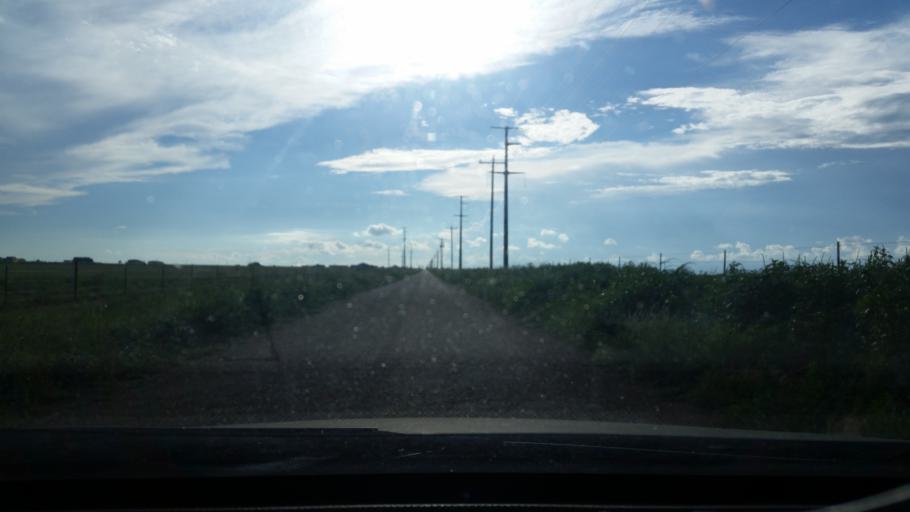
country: US
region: New Mexico
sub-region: Curry County
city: Clovis
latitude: 34.5065
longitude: -103.1844
